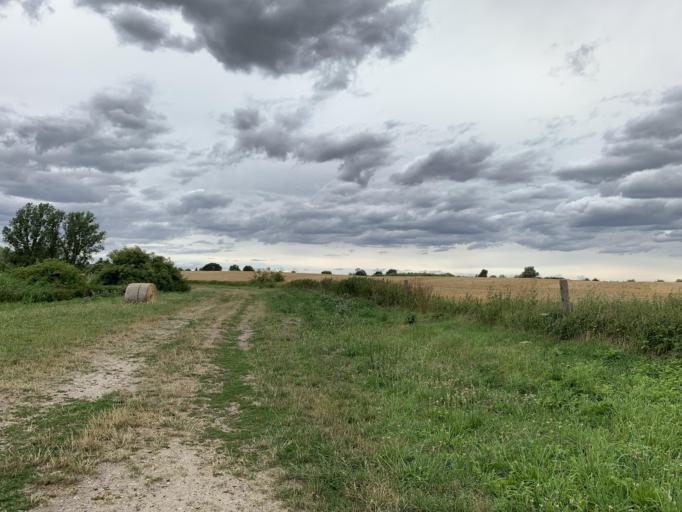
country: DE
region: Mecklenburg-Vorpommern
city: Blankensee
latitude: 53.3912
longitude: 13.2392
